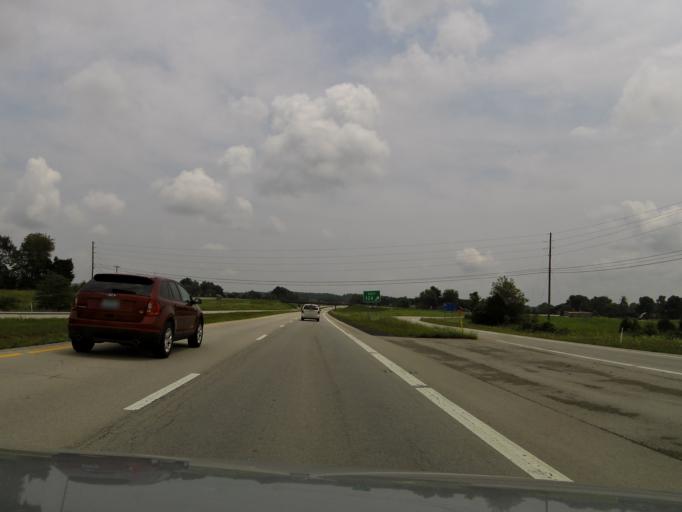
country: US
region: Kentucky
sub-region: Hardin County
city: Elizabethtown
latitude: 37.5696
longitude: -86.0420
